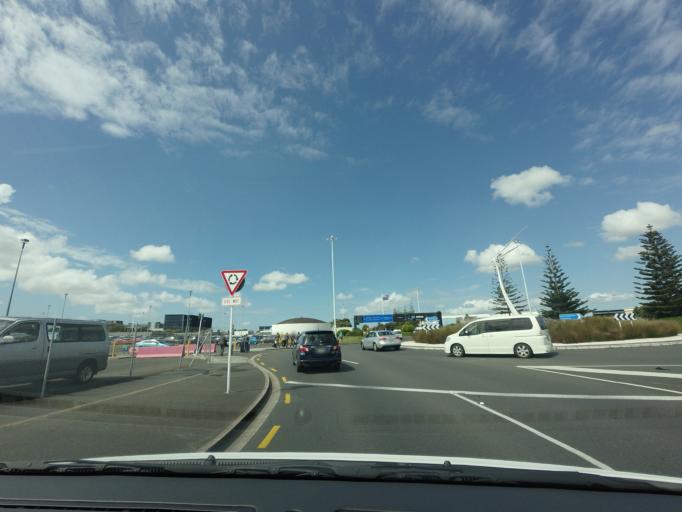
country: NZ
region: Auckland
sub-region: Auckland
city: Mangere
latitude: -37.0024
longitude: 174.7860
